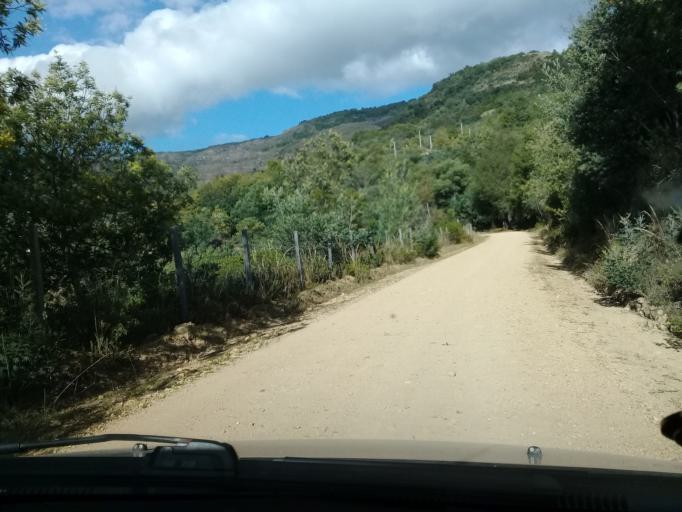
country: CO
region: Cundinamarca
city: Guatavita
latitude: 4.9420
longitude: -73.8672
